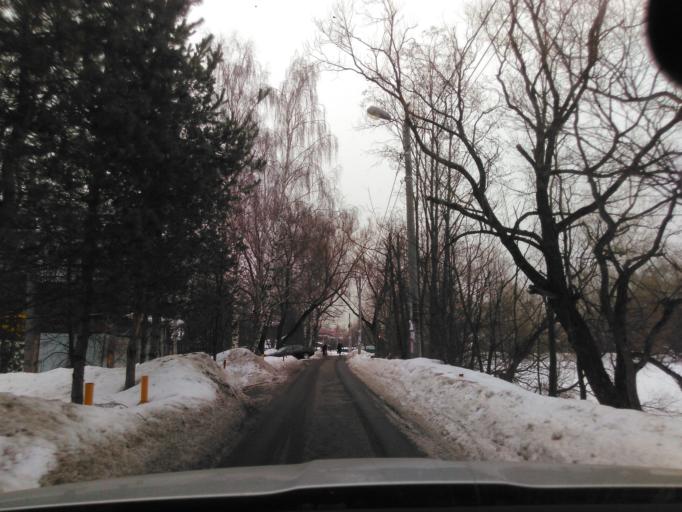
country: RU
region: Moscow
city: Khimki
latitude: 55.8884
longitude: 37.3867
